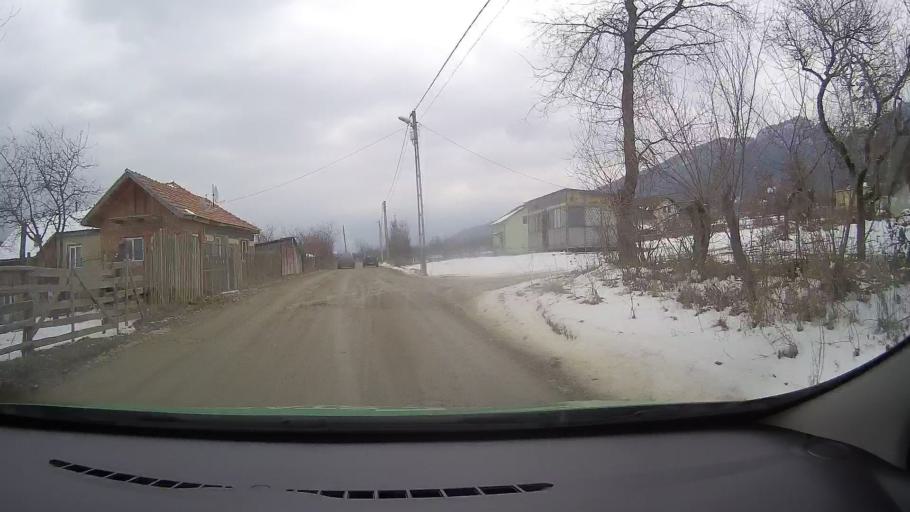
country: RO
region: Brasov
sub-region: Comuna Zarnesti
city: Zarnesti
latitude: 45.5441
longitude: 25.3232
